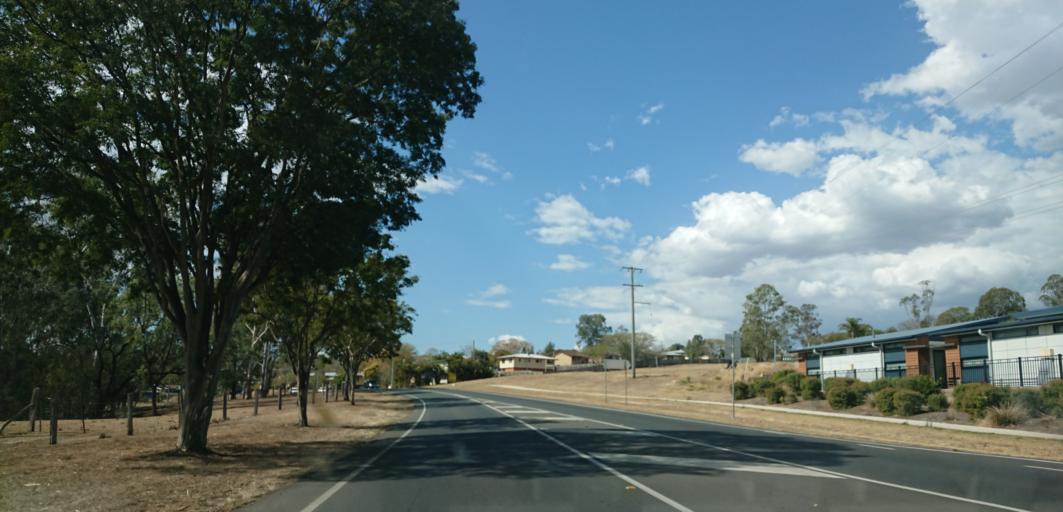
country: AU
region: Queensland
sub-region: Lockyer Valley
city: Gatton
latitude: -27.5685
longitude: 152.2702
